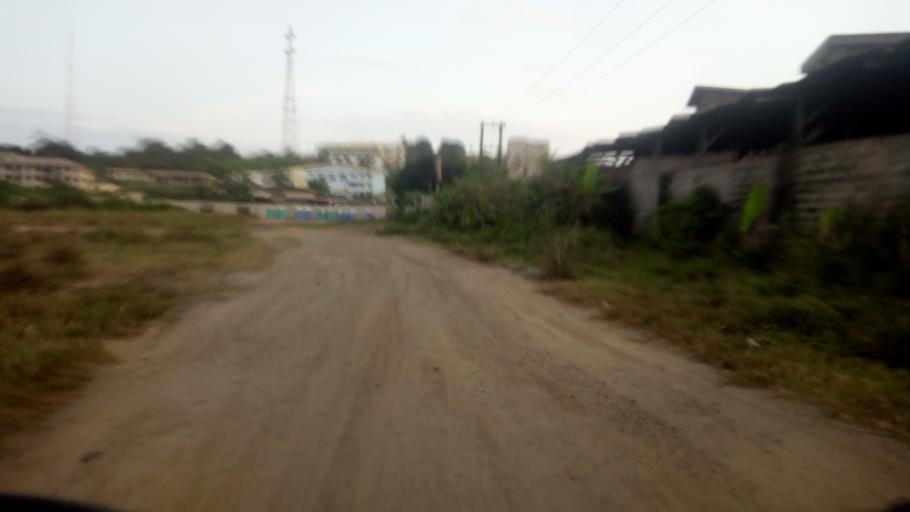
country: GH
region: Central
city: Cape Coast
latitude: 5.1163
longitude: -1.2768
